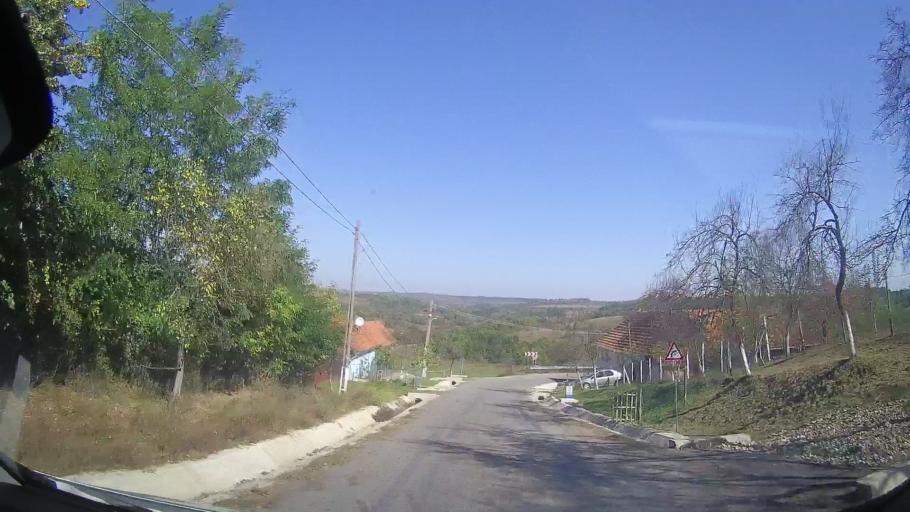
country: RO
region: Timis
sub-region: Comuna Ohaba Lunga
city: Ohaba Lunga
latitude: 45.9115
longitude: 21.9413
